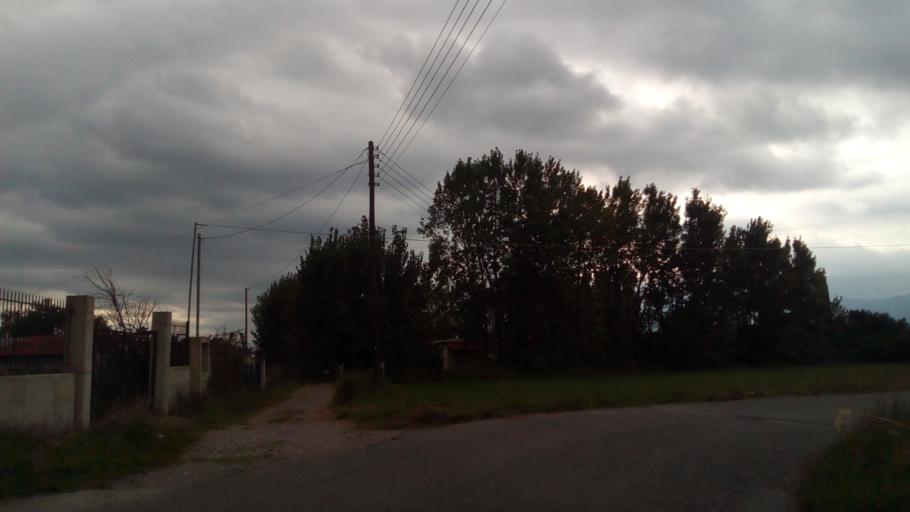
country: GR
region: West Greece
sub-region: Nomos Aitolias kai Akarnanias
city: Nafpaktos
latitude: 38.3987
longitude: 21.9139
